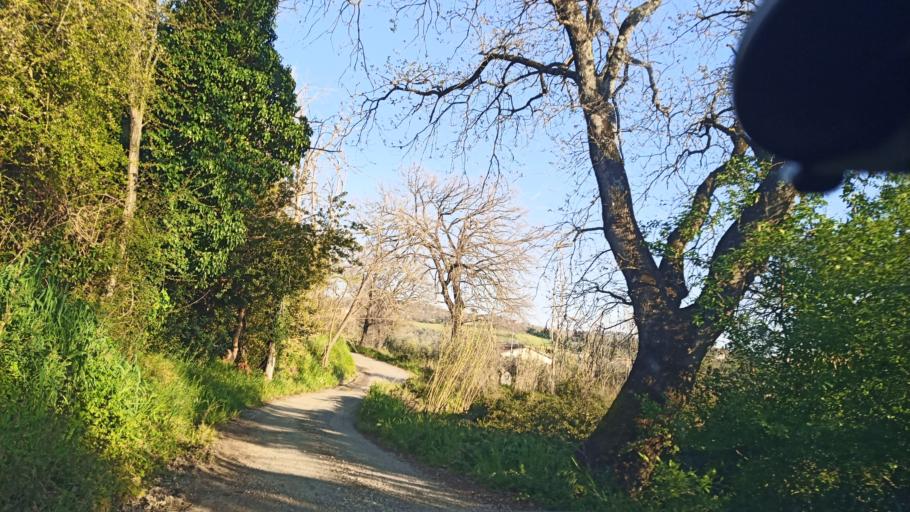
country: IT
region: Latium
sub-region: Provincia di Rieti
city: Poggio Mirteto
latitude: 42.2641
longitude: 12.6622
